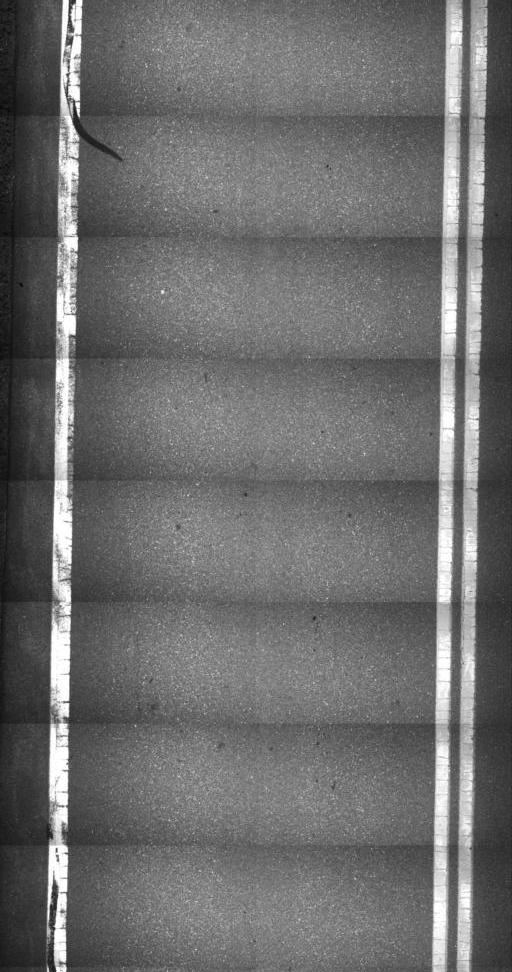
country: US
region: Massachusetts
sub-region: Franklin County
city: Bernardston
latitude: 42.7359
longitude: -72.5718
